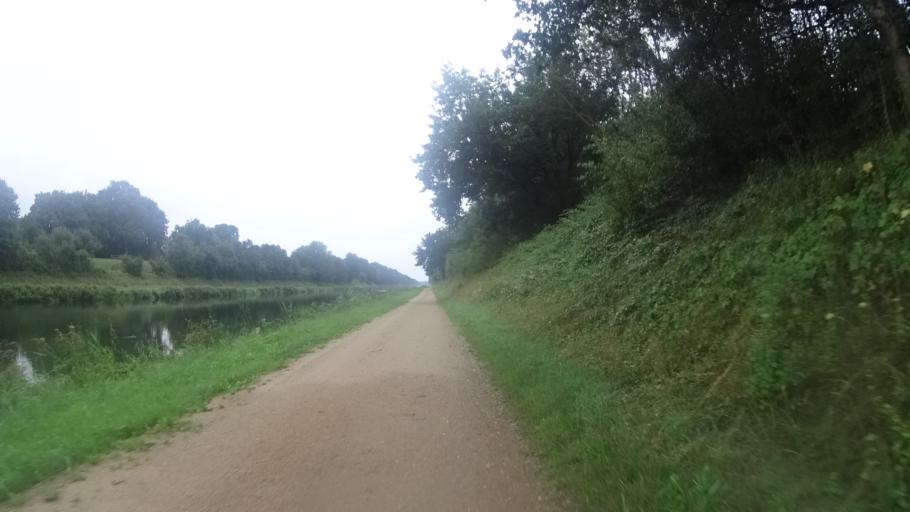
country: DE
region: Schleswig-Holstein
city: Grambek
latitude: 53.5777
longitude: 10.6740
